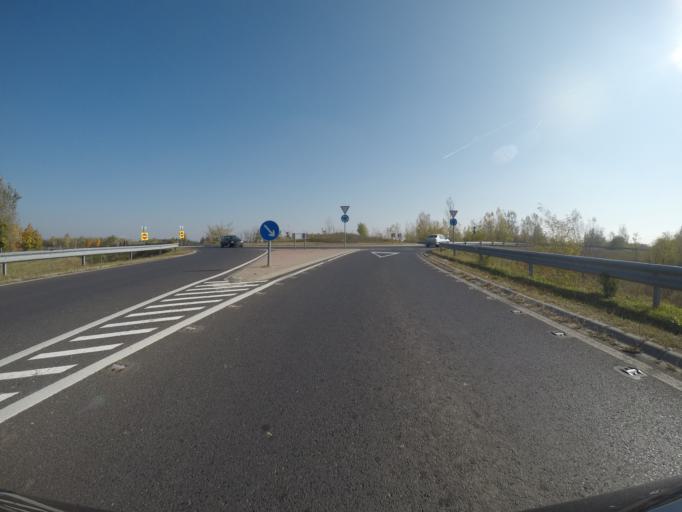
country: HU
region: Tolna
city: Paks
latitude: 46.6020
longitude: 18.8190
